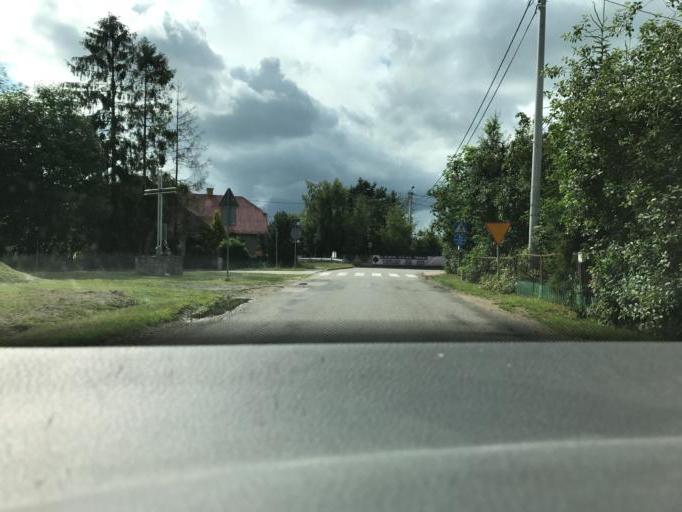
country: PL
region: Pomeranian Voivodeship
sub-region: Powiat gdanski
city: Pruszcz Gdanski
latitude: 54.2942
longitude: 18.7213
